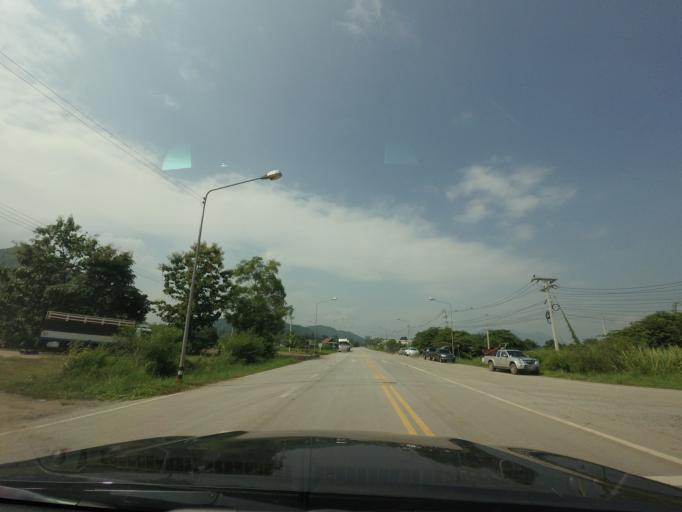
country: LA
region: Xiagnabouli
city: Muang Kenthao
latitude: 17.6857
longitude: 101.3923
